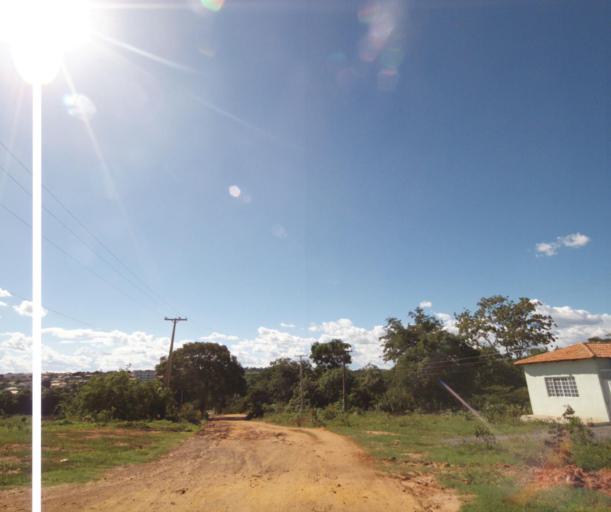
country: BR
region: Bahia
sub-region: Carinhanha
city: Carinhanha
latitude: -14.1793
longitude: -44.5270
